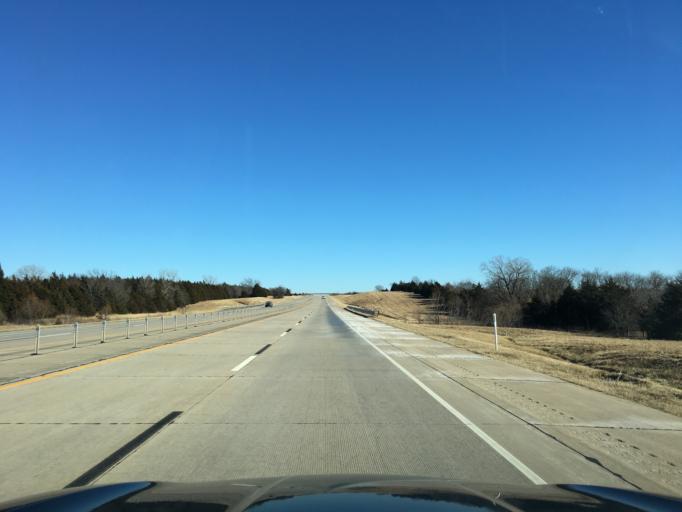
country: US
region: Oklahoma
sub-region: Payne County
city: Yale
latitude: 36.2250
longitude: -96.6774
